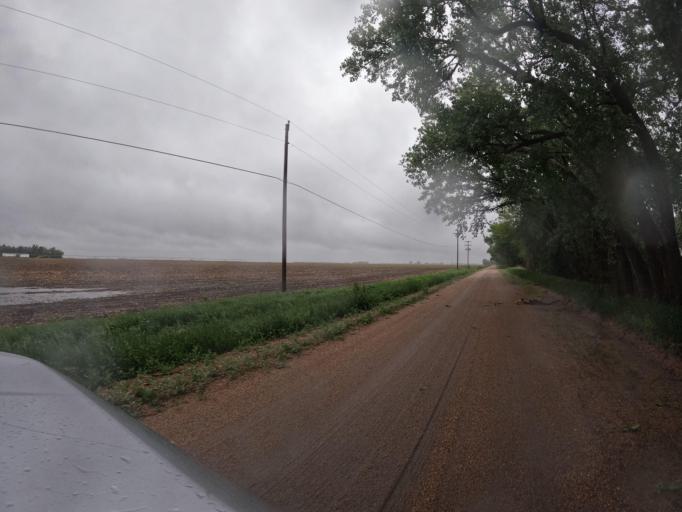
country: US
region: Nebraska
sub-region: Clay County
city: Harvard
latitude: 40.6192
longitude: -98.1040
